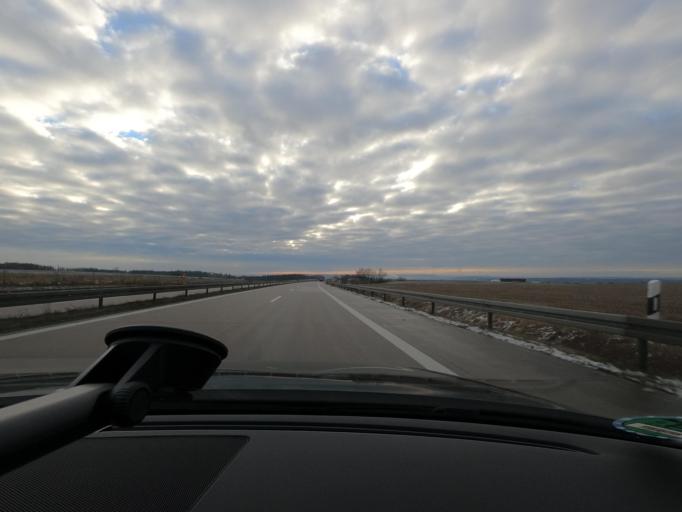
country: DE
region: Bavaria
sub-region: Upper Franconia
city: Meeder
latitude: 50.3372
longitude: 10.9346
